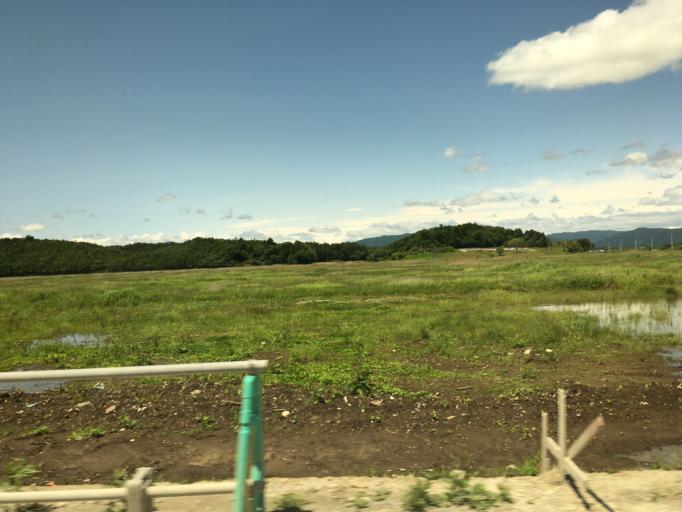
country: JP
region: Fukushima
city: Namie
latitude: 37.4798
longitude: 141.0294
